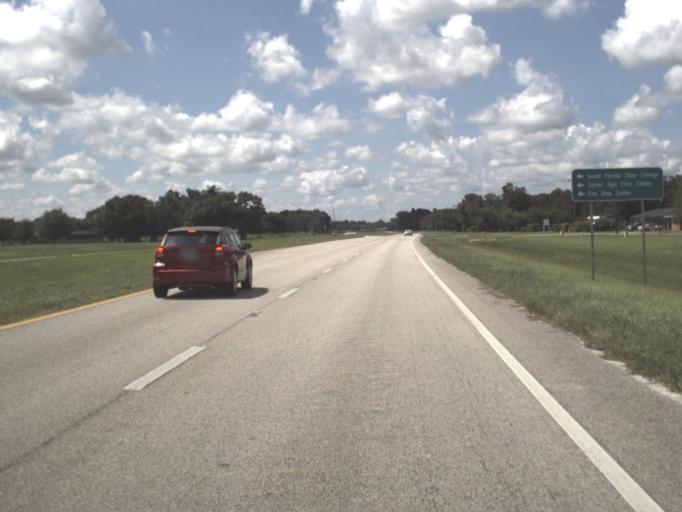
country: US
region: Florida
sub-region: DeSoto County
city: Arcadia
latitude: 27.2596
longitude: -81.8409
